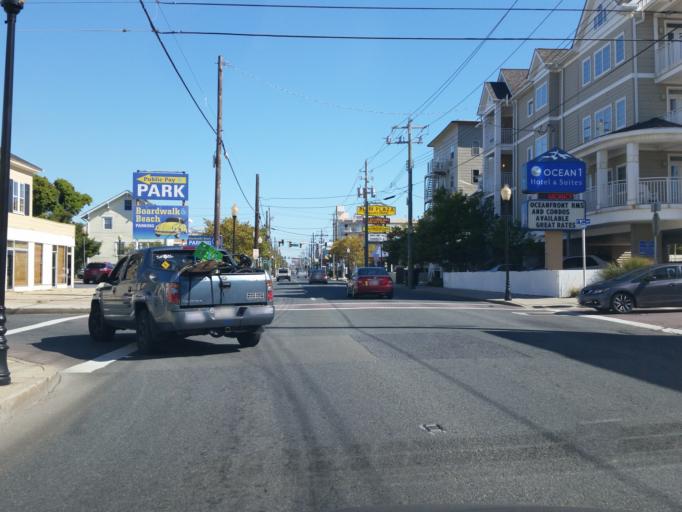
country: US
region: Maryland
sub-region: Worcester County
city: Ocean City
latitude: 38.3325
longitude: -75.0857
